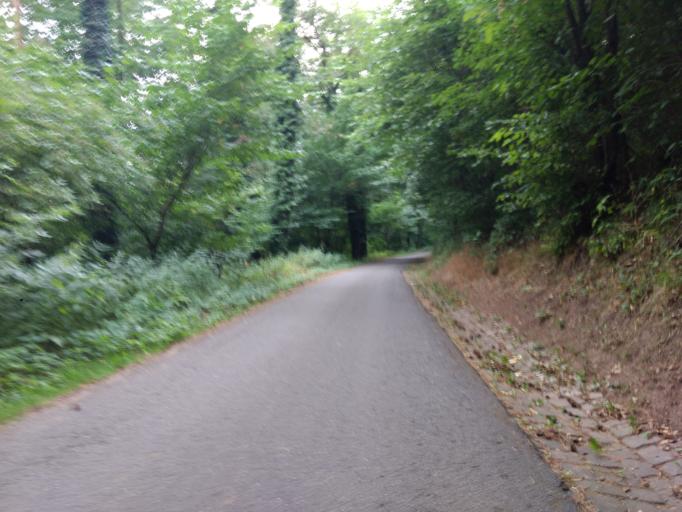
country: DE
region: Saarland
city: Wallerfangen
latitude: 49.3344
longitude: 6.6945
